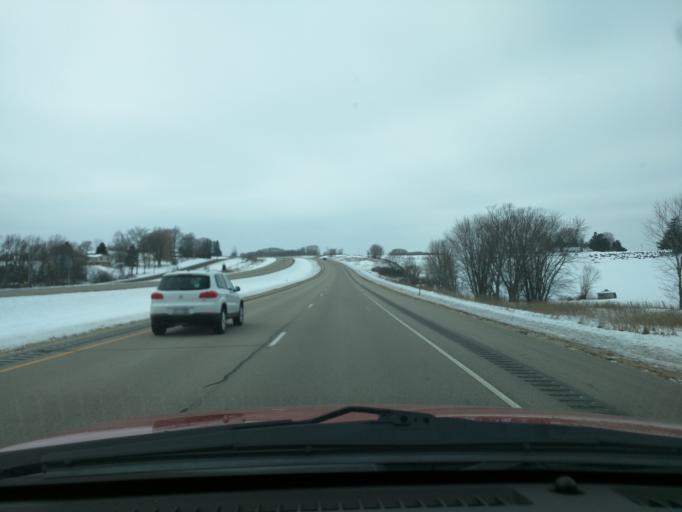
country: US
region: Wisconsin
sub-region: Trempealeau County
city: Trempealeau
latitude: 43.9200
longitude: -91.5003
